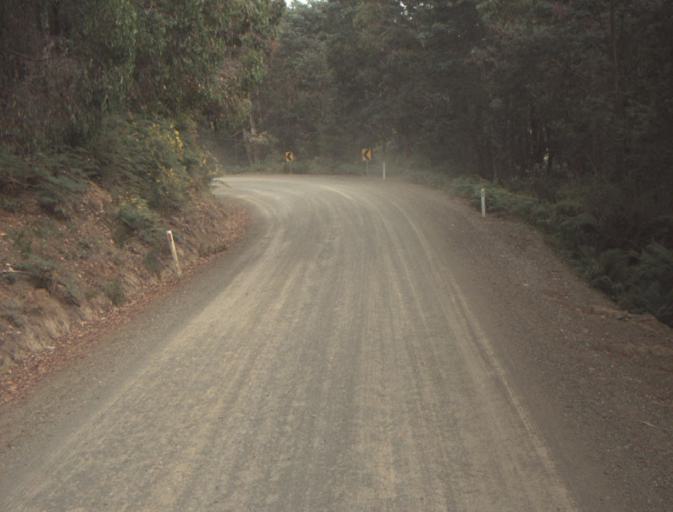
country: AU
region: Tasmania
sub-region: Dorset
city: Scottsdale
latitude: -41.3280
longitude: 147.4252
